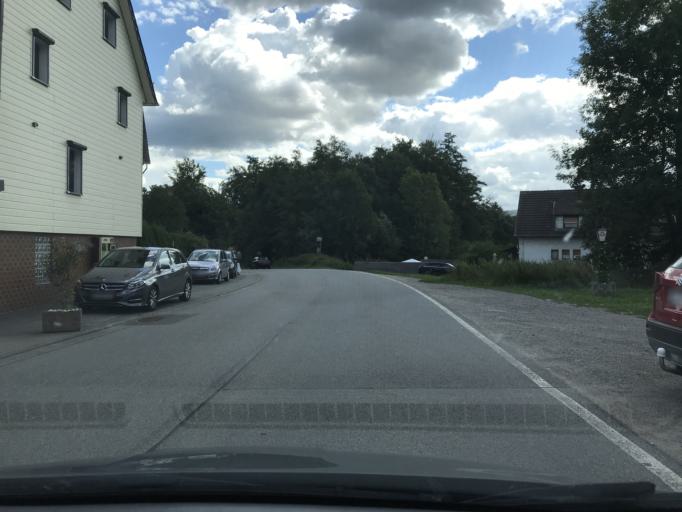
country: DE
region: Hesse
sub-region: Regierungsbezirk Darmstadt
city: Furth
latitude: 49.6568
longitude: 8.7526
